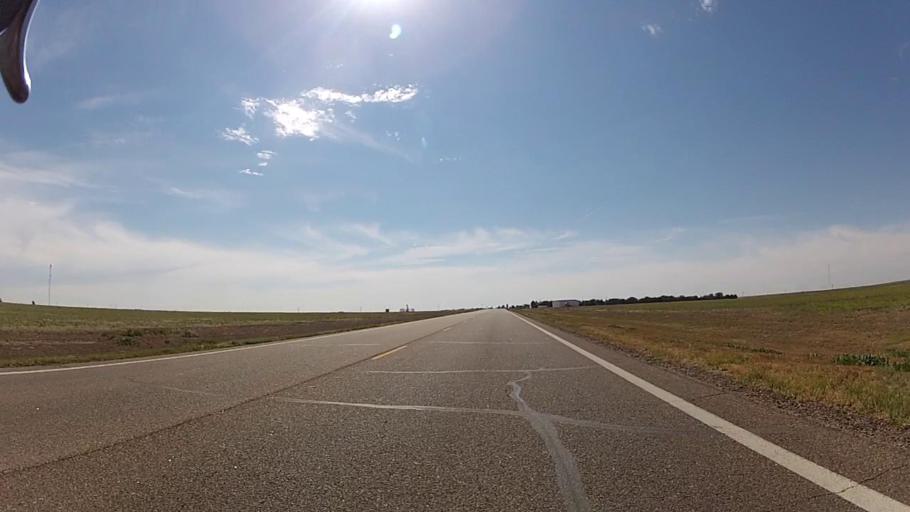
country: US
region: Kansas
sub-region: Grant County
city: Ulysses
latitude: 37.5660
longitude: -101.3157
